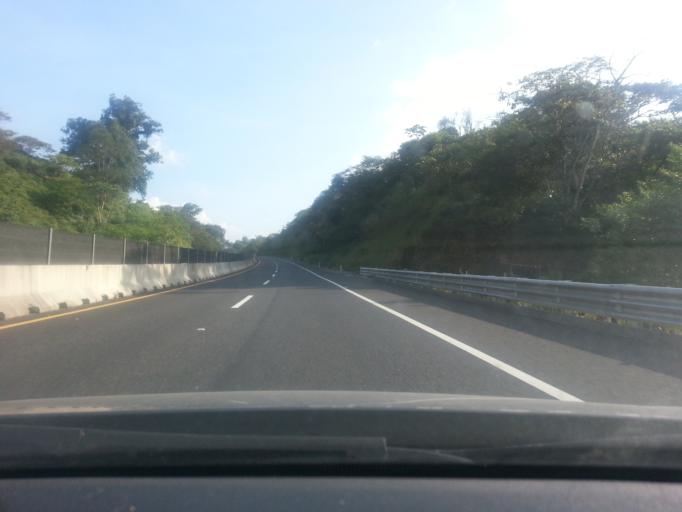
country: MX
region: Puebla
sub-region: Xicotepec
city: San Lorenzo
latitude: 20.4030
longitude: -97.9426
